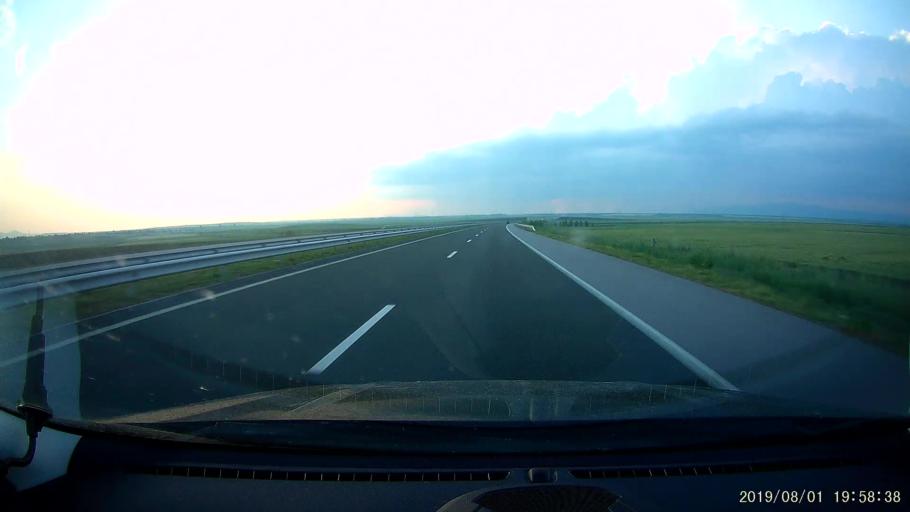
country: BG
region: Yambol
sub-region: Obshtina Straldzha
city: Straldzha
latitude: 42.5454
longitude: 26.7580
